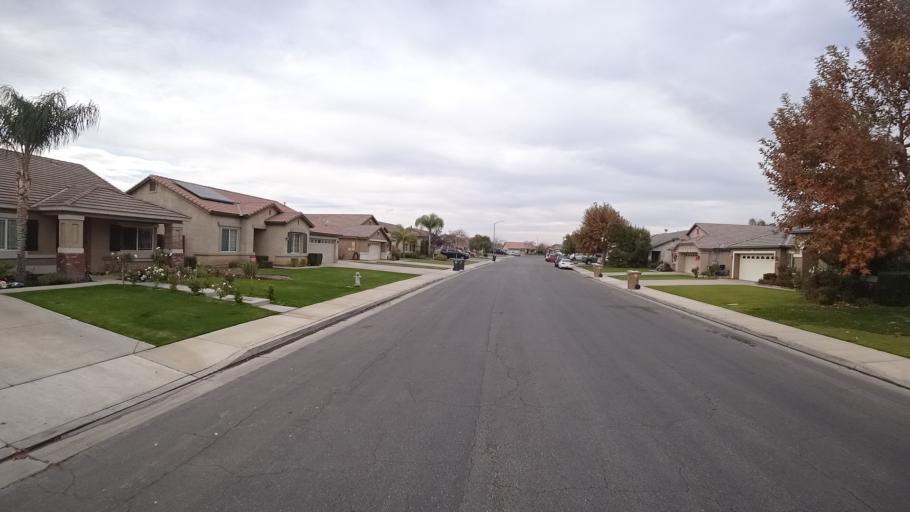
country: US
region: California
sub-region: Kern County
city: Rosedale
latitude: 35.4070
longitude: -119.1511
